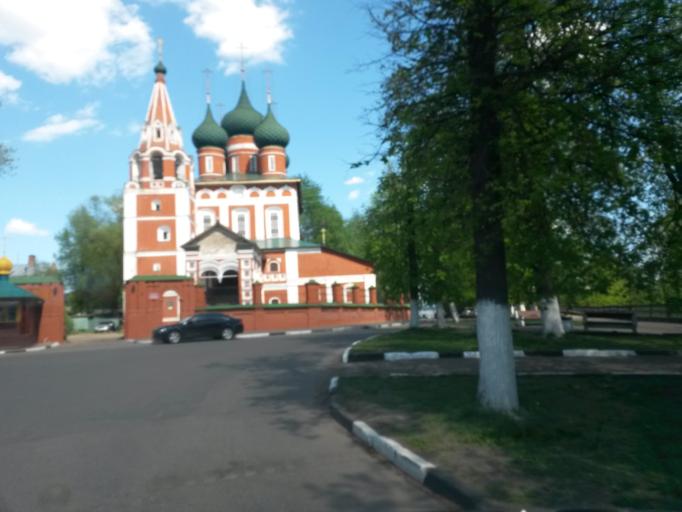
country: RU
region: Jaroslavl
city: Yaroslavl
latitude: 57.6217
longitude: 39.8917
